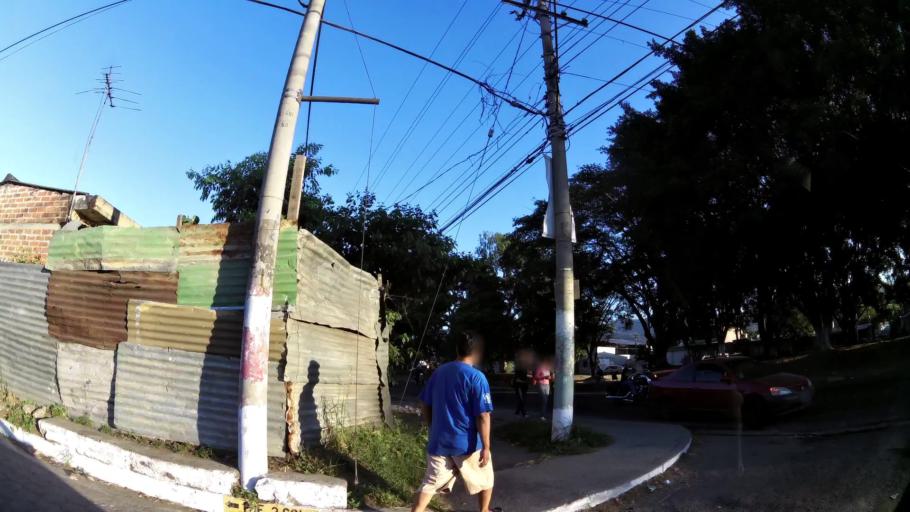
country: SV
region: La Libertad
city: Santa Tecla
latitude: 13.7205
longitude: -89.3620
